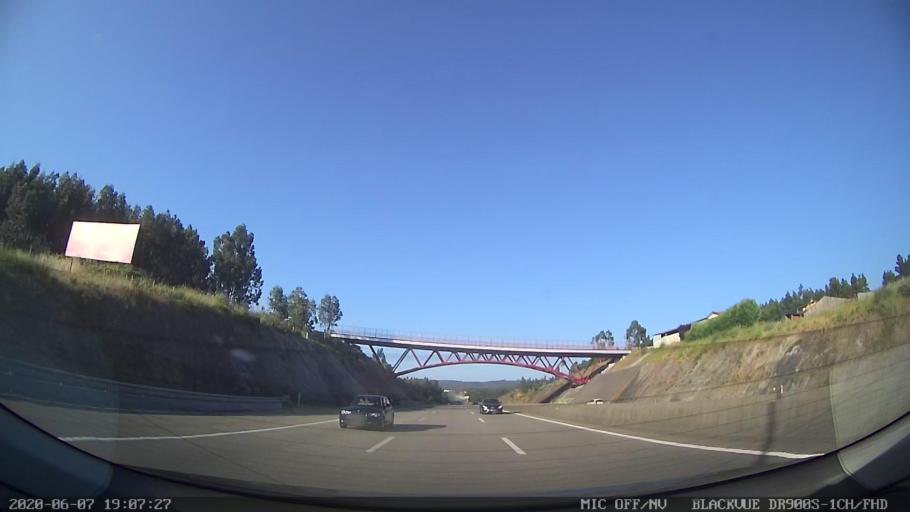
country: PT
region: Porto
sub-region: Trofa
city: Sao Romao do Coronado
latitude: 41.2889
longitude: -8.5527
